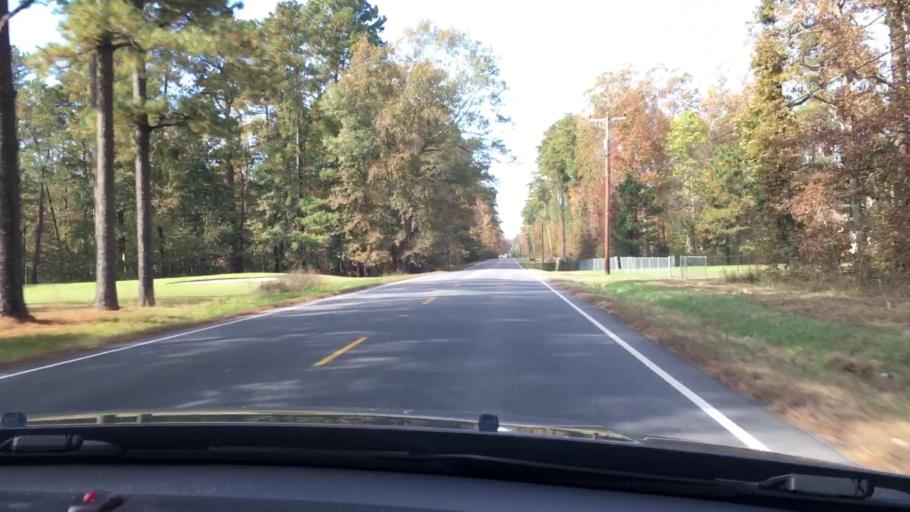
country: US
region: Virginia
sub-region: King William County
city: West Point
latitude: 37.5644
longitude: -76.8276
